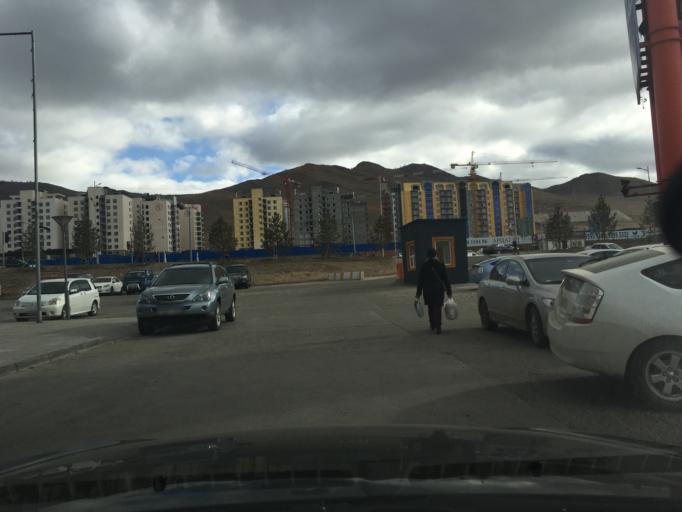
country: MN
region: Ulaanbaatar
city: Ulaanbaatar
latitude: 47.8781
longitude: 106.8505
